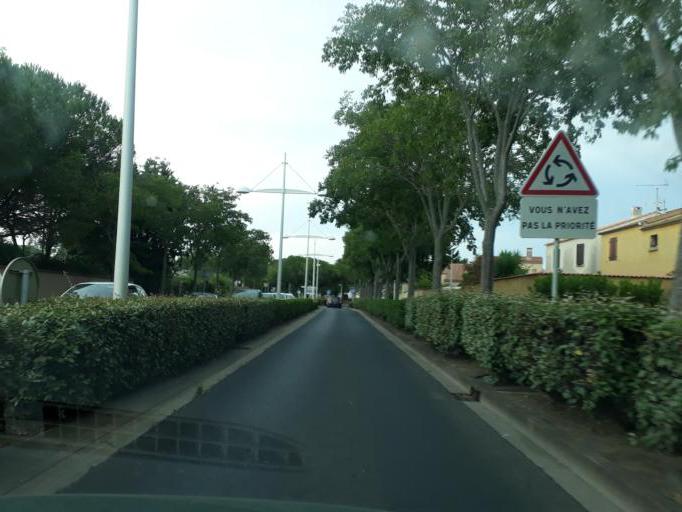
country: FR
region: Languedoc-Roussillon
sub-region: Departement de l'Herault
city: Agde
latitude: 43.3001
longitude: 3.4802
